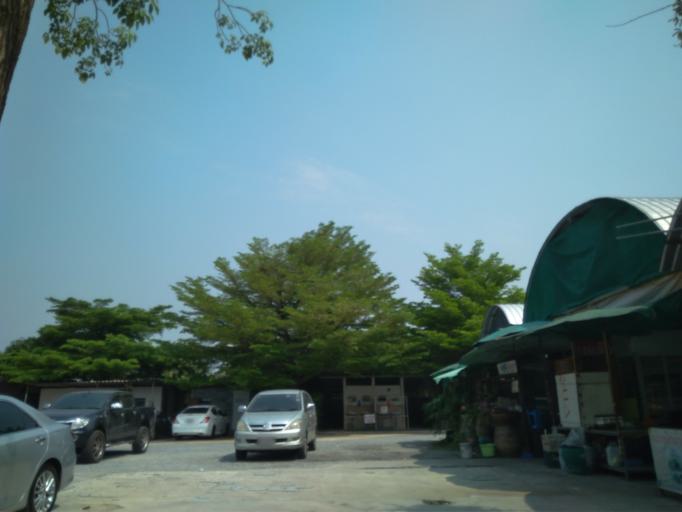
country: TH
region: Bangkok
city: Taling Chan
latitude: 13.7786
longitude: 100.4541
